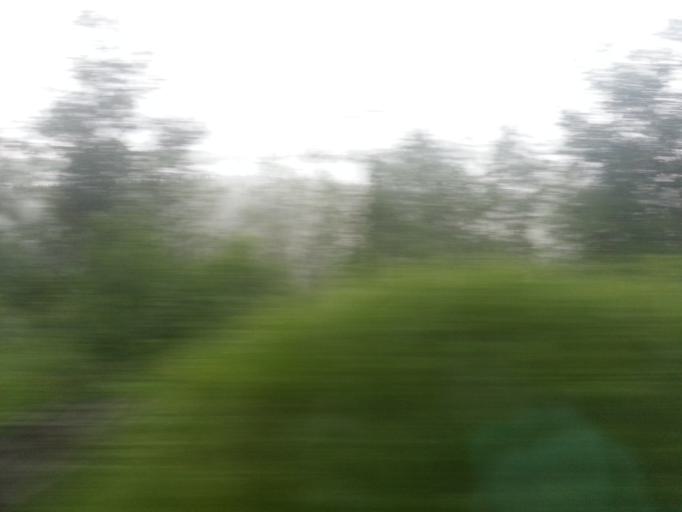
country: NO
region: Sor-Trondelag
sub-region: Midtre Gauldal
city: Storen
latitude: 62.9771
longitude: 10.2042
